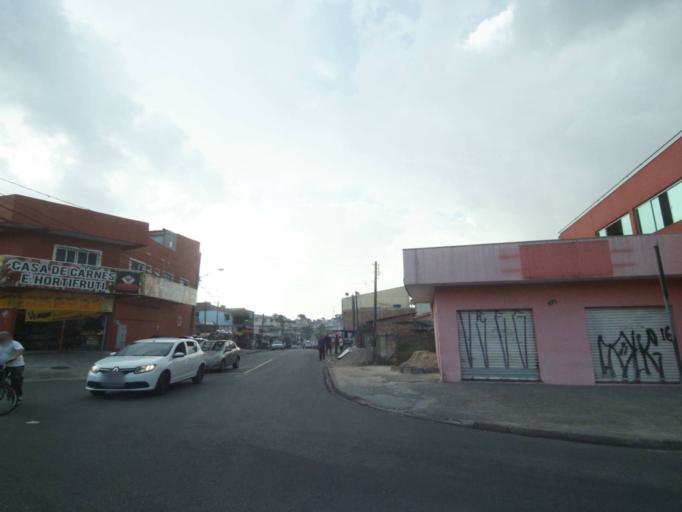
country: BR
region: Parana
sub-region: Sao Jose Dos Pinhais
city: Sao Jose dos Pinhais
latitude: -25.5345
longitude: -49.2776
